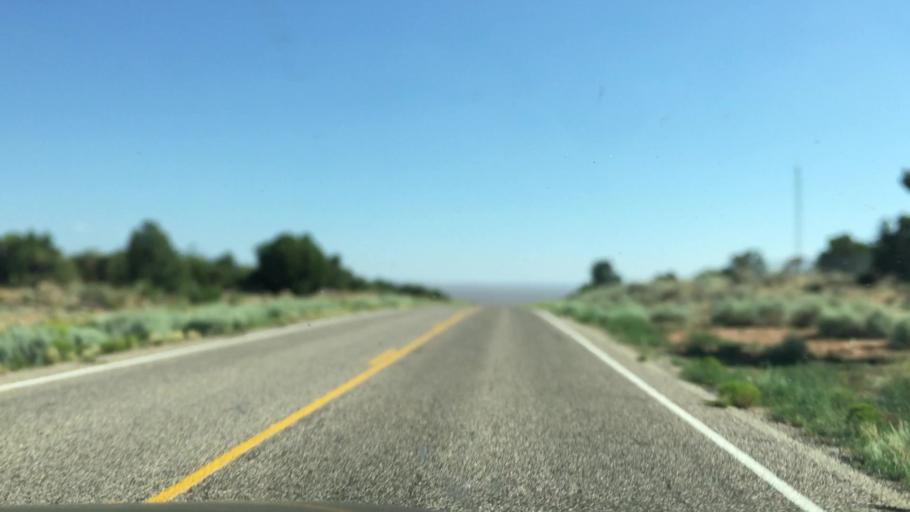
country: US
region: Arizona
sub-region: Coconino County
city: Fredonia
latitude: 36.8737
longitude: -112.7383
